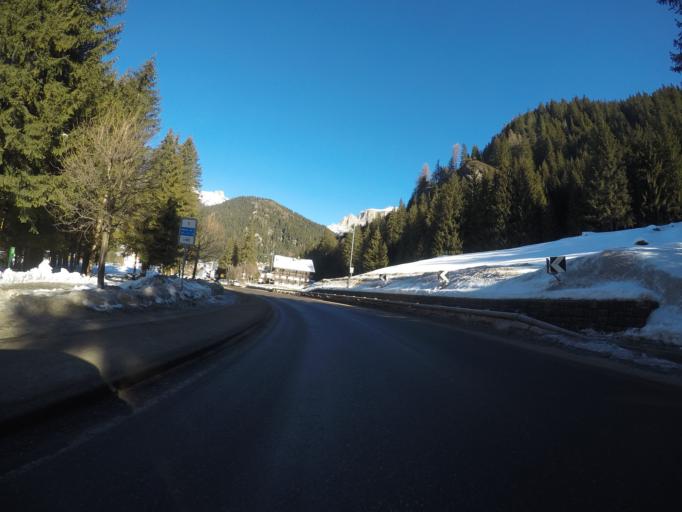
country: IT
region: Trentino-Alto Adige
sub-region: Provincia di Trento
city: Canazei
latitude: 46.4704
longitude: 11.7787
